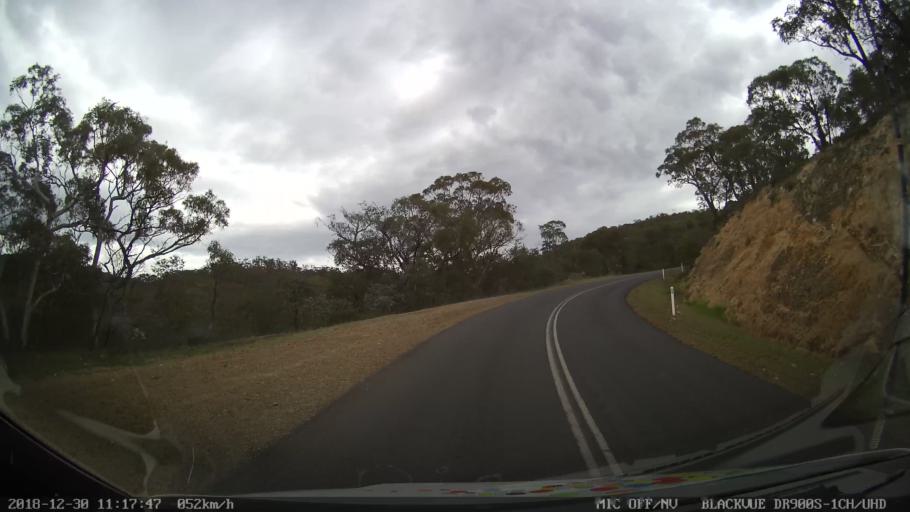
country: AU
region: New South Wales
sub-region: Snowy River
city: Jindabyne
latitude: -36.5365
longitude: 148.6957
